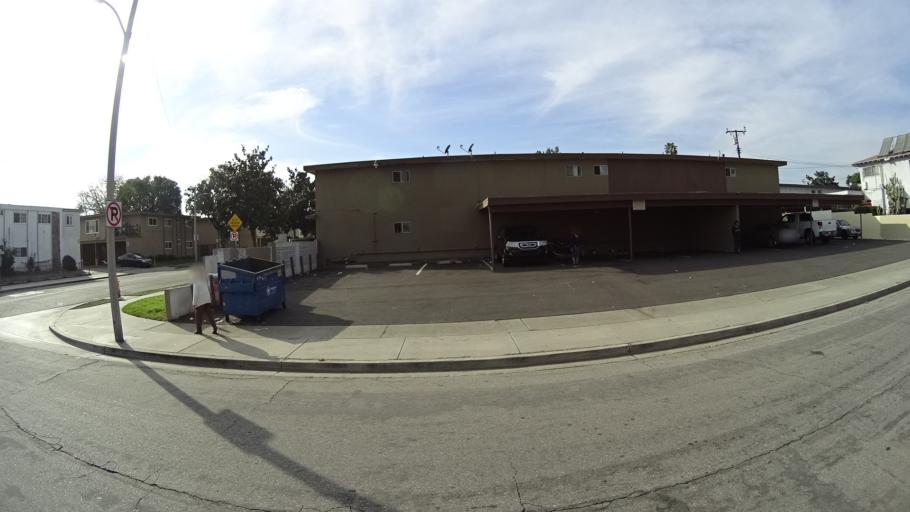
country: US
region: California
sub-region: Orange County
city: Garden Grove
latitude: 33.7578
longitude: -117.9078
